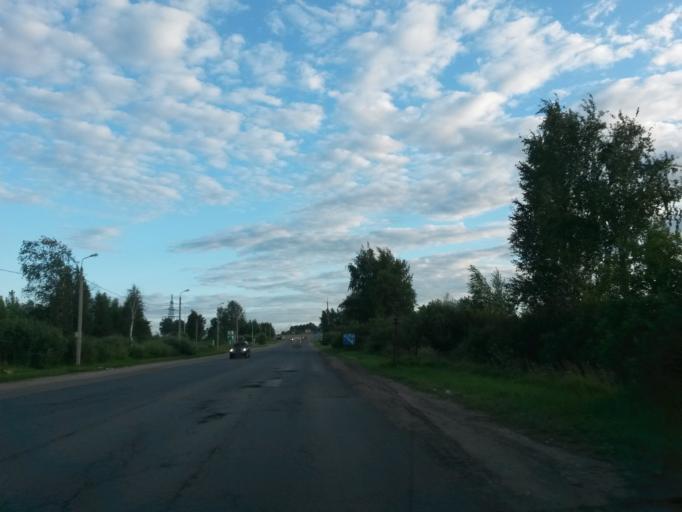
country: RU
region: Jaroslavl
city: Yaroslavl
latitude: 57.5624
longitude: 39.8569
